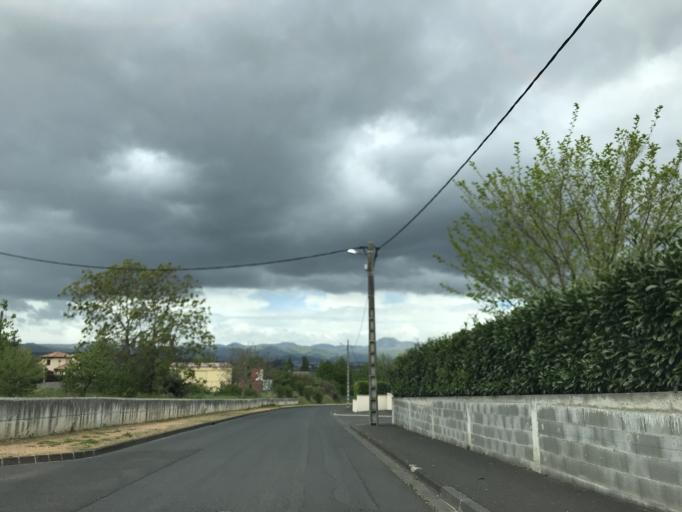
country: FR
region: Auvergne
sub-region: Departement du Puy-de-Dome
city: Pont-du-Chateau
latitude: 45.7932
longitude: 3.2314
